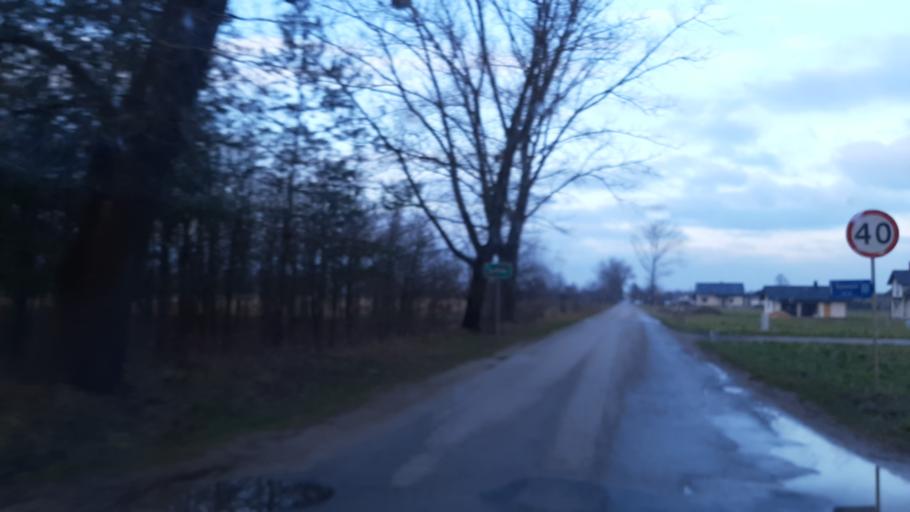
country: PL
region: Lublin Voivodeship
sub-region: Powiat lubelski
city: Garbow
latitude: 51.3961
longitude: 22.4097
